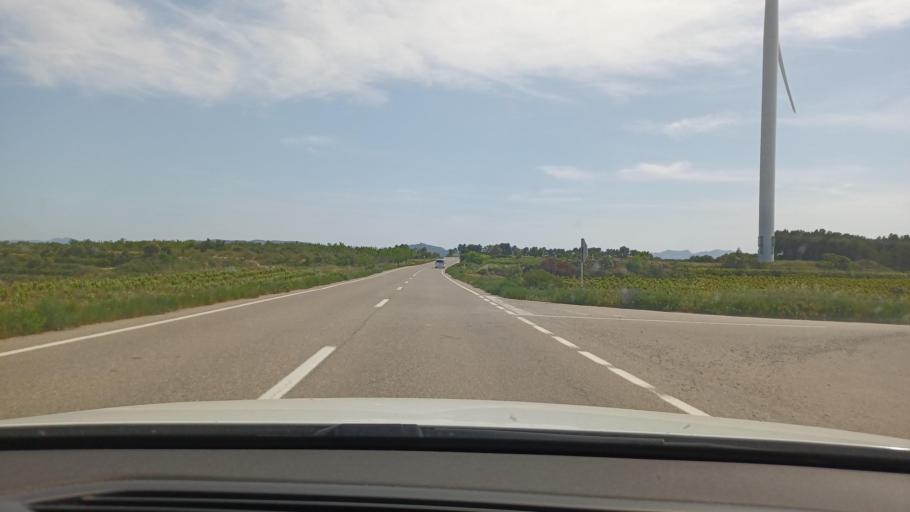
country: ES
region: Catalonia
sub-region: Provincia de Tarragona
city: Vilalba dels Arcs
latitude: 41.0973
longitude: 0.4179
